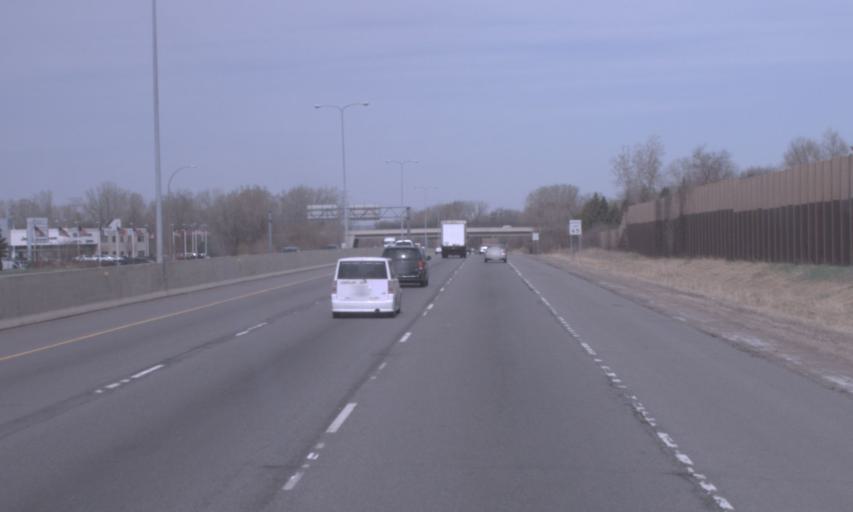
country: US
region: Minnesota
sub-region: Anoka County
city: Coon Rapids
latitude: 45.1593
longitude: -93.2813
